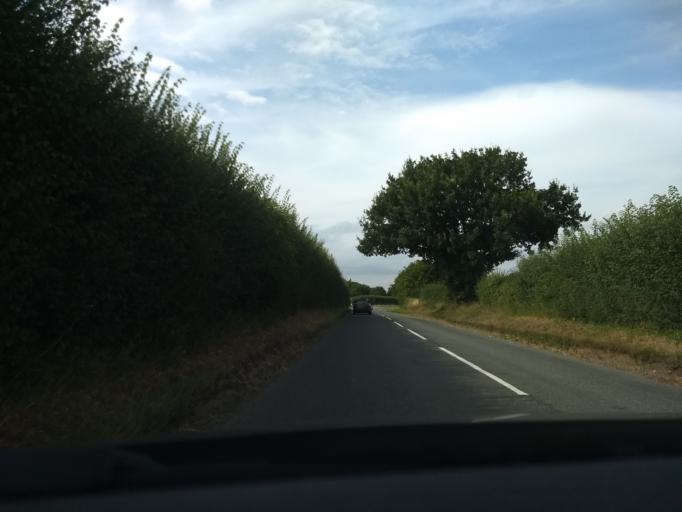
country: GB
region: England
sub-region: Suffolk
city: Ipswich
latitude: 52.0090
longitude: 1.1658
